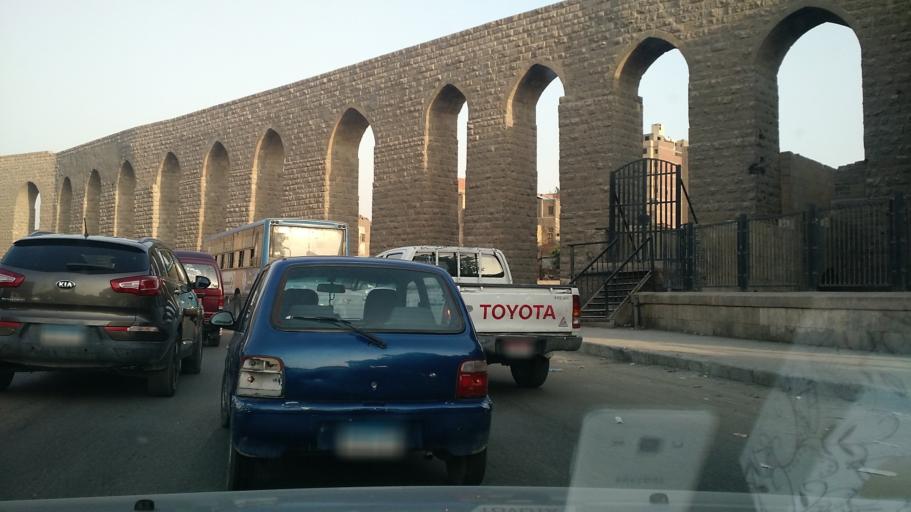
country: EG
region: Al Jizah
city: Al Jizah
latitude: 30.0224
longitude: 31.2305
